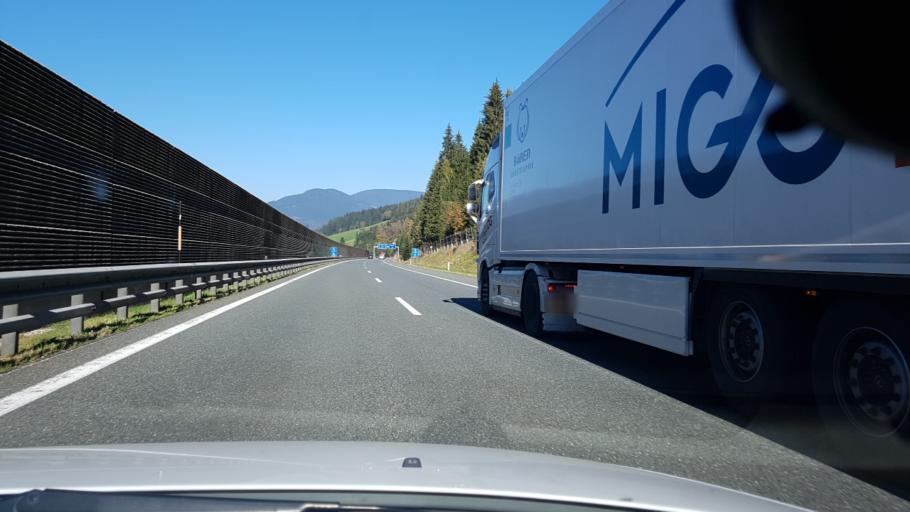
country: AT
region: Salzburg
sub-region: Politischer Bezirk Sankt Johann im Pongau
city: Flachau
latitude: 47.3526
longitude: 13.3972
